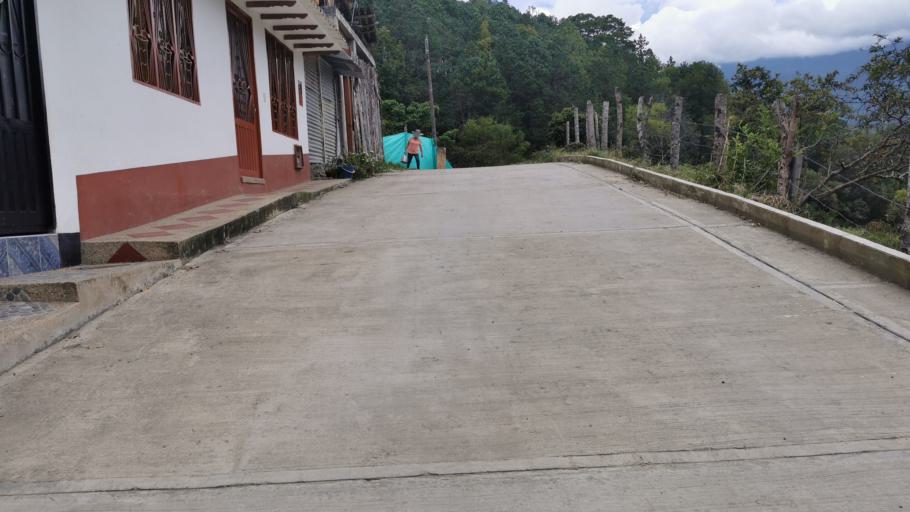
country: CO
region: Cundinamarca
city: Tenza
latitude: 5.0772
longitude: -73.4244
